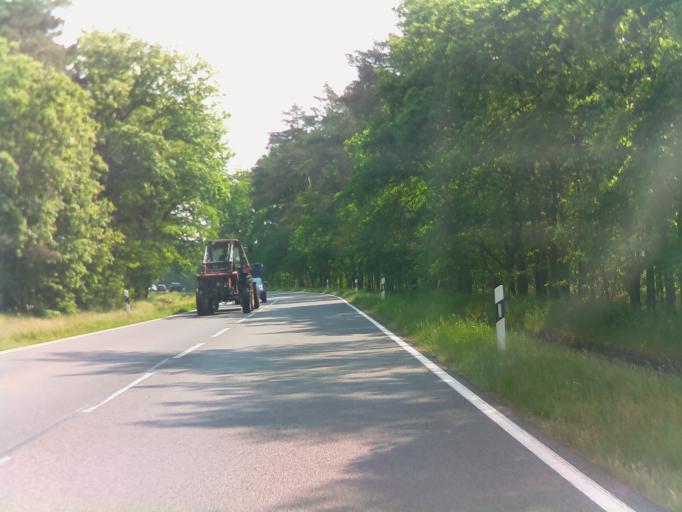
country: DE
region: Saxony-Anhalt
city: Schonhausen
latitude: 52.5466
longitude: 12.0441
